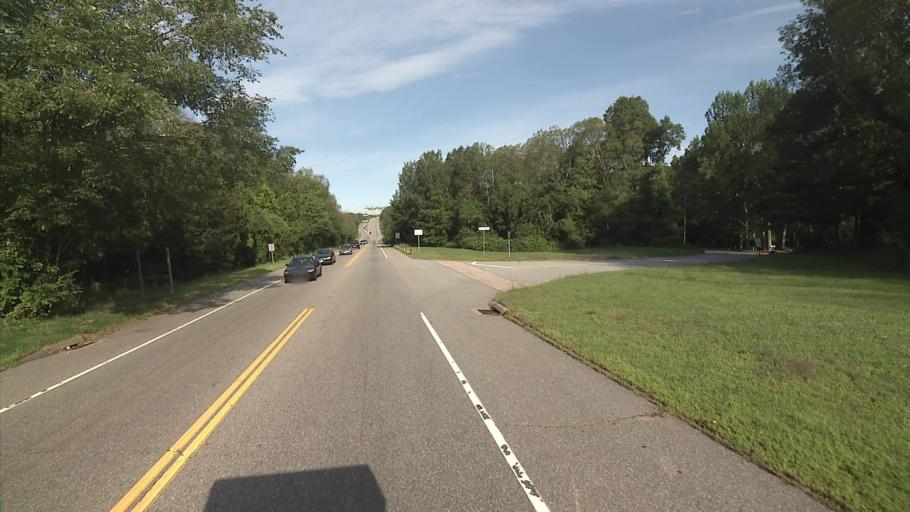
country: US
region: Connecticut
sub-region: New London County
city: Preston City
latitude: 41.4672
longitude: -71.9391
